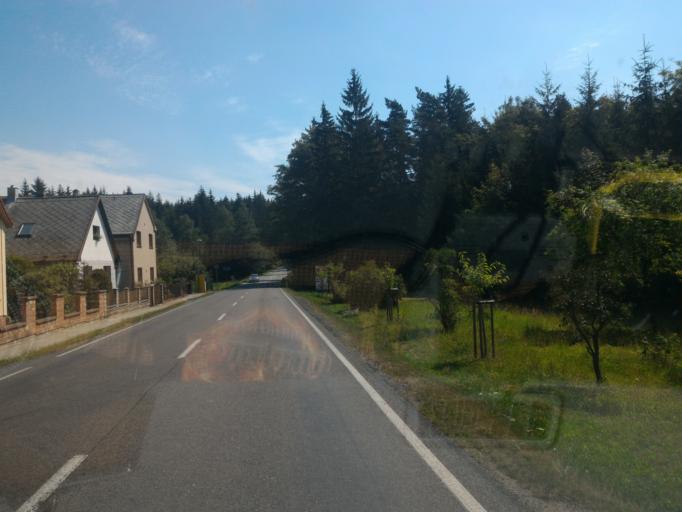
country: CZ
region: Pardubicky
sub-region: Okres Chrudim
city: Hlinsko
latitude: 49.7696
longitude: 15.8615
